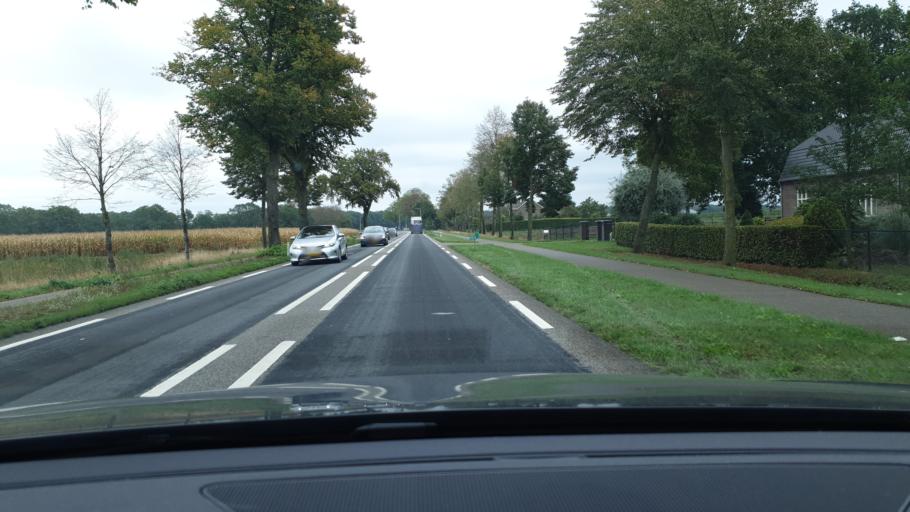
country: NL
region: Limburg
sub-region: Gemeente Bergen
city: Wellerlooi
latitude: 51.5292
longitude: 6.0571
